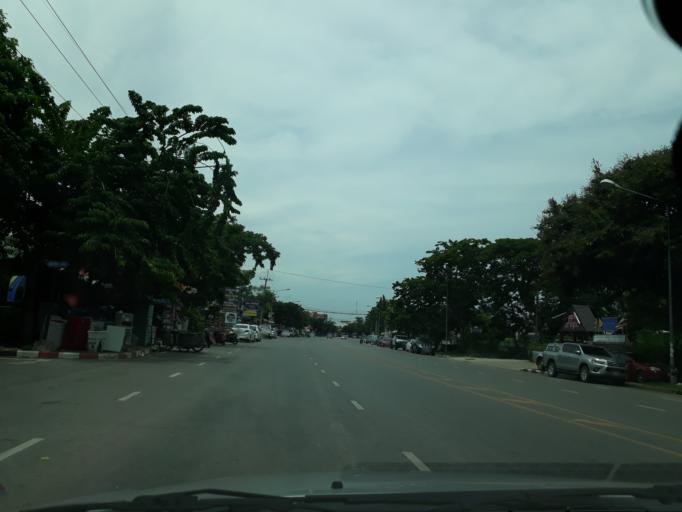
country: TH
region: Khon Kaen
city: Khon Kaen
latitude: 16.4334
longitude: 102.8651
